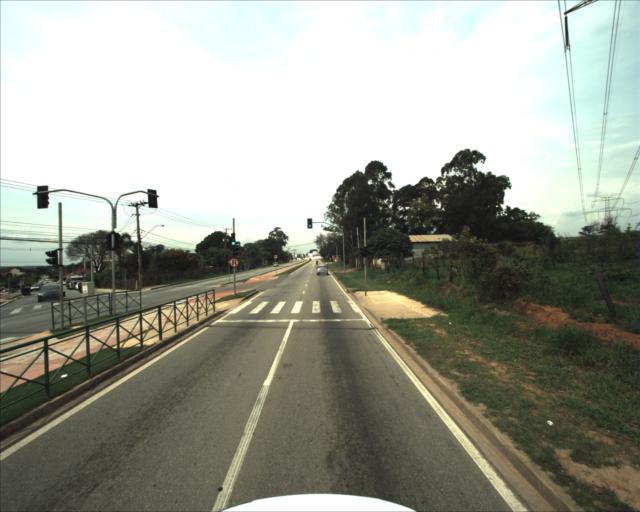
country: BR
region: Sao Paulo
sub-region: Sorocaba
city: Sorocaba
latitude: -23.4254
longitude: -47.4205
